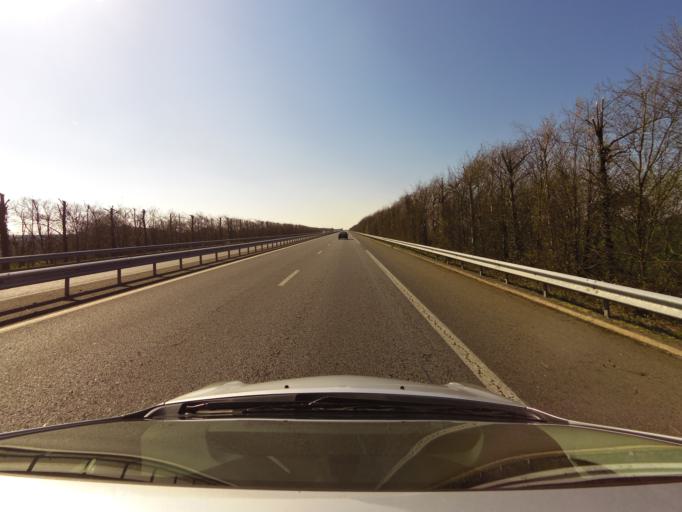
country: FR
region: Brittany
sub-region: Departement d'Ille-et-Vilaine
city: Plelan-le-Grand
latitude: 47.9828
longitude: -2.0981
